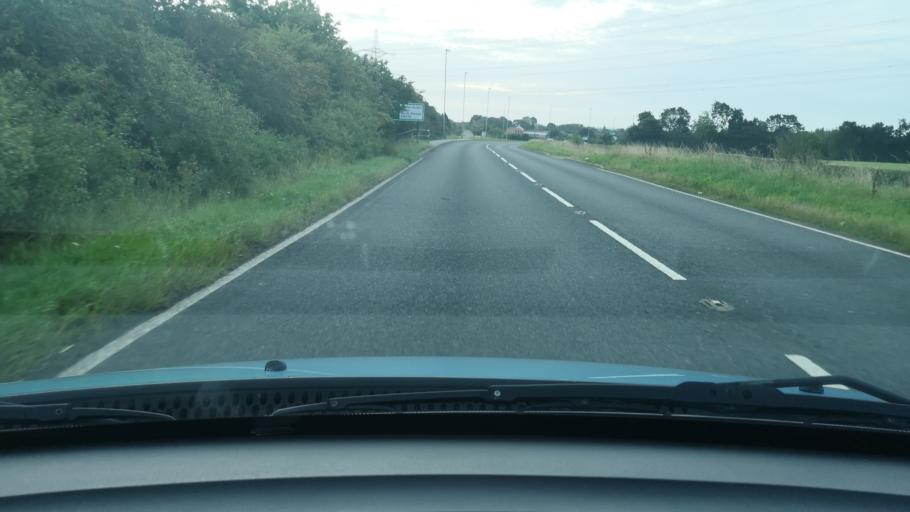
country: GB
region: England
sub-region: City and Borough of Wakefield
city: Upton
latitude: 53.6116
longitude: -1.2906
